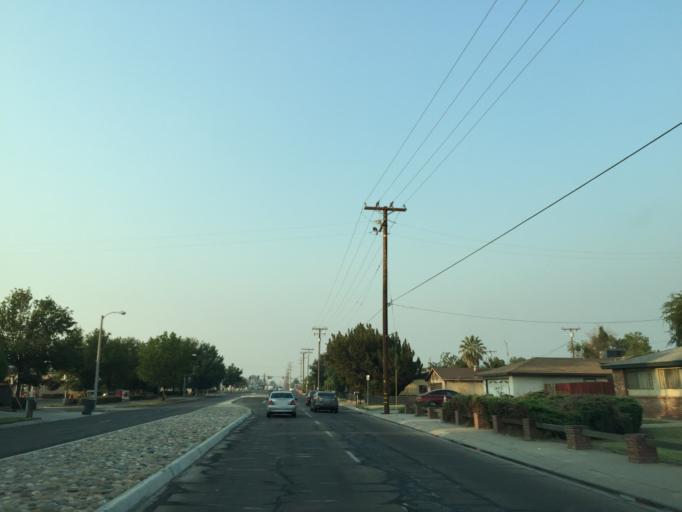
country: US
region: California
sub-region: Tulare County
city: Visalia
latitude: 36.3446
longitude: -119.2789
